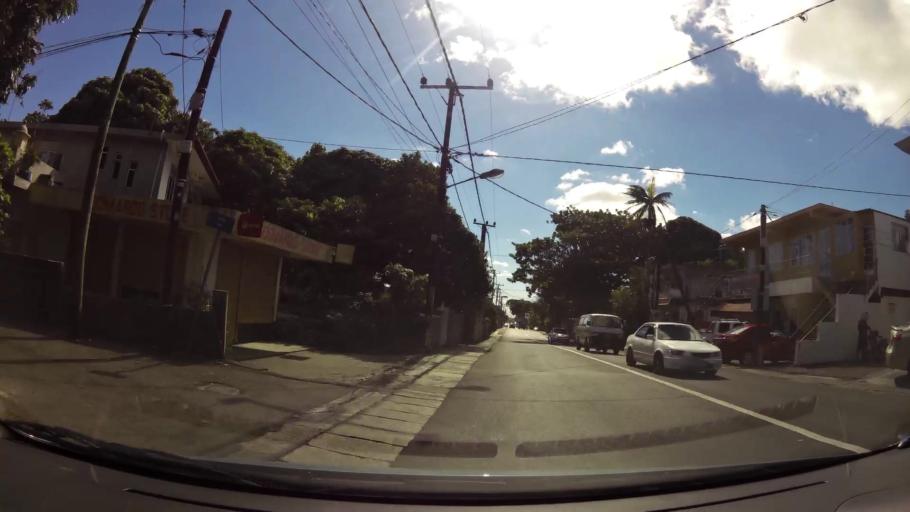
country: MU
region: Plaines Wilhems
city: Vacoas
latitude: -20.2834
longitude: 57.4794
